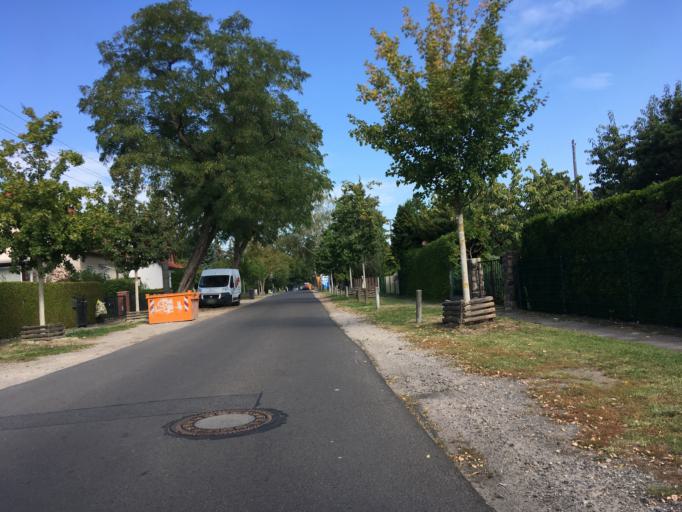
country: DE
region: Berlin
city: Kaulsdorf
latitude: 52.5217
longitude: 13.5968
